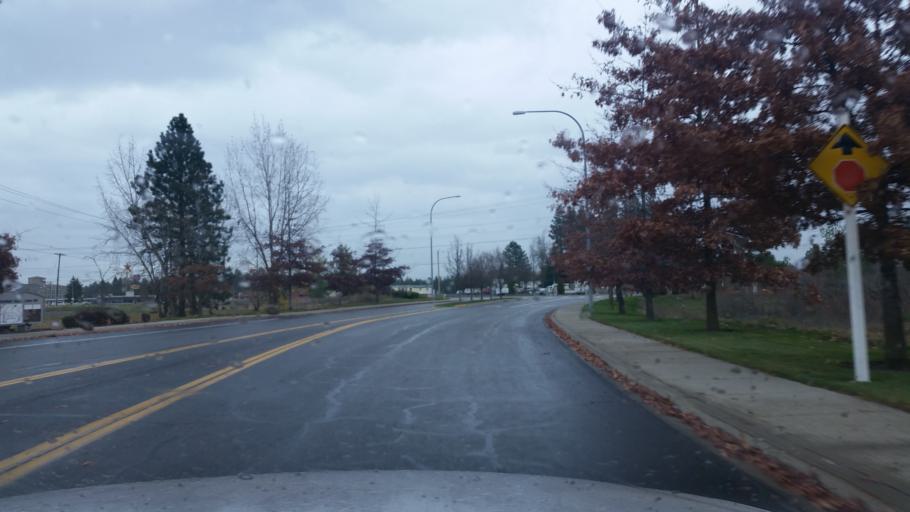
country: US
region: Washington
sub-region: Spokane County
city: Airway Heights
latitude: 47.6190
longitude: -117.5112
